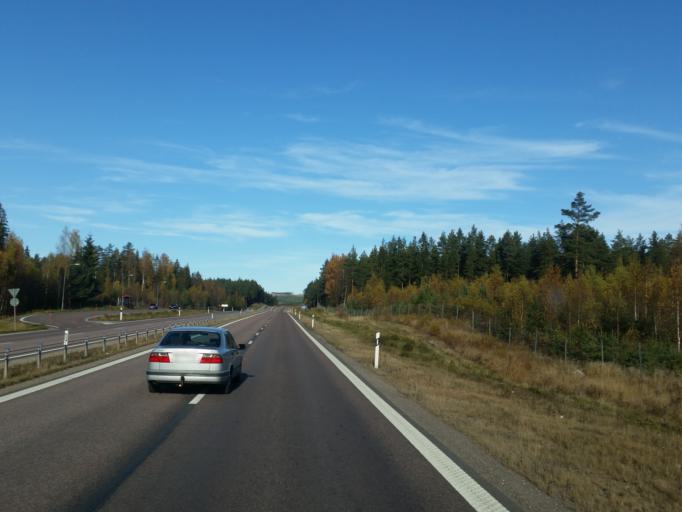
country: SE
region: Dalarna
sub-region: Borlange Kommun
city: Ornas
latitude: 60.5236
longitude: 15.5531
